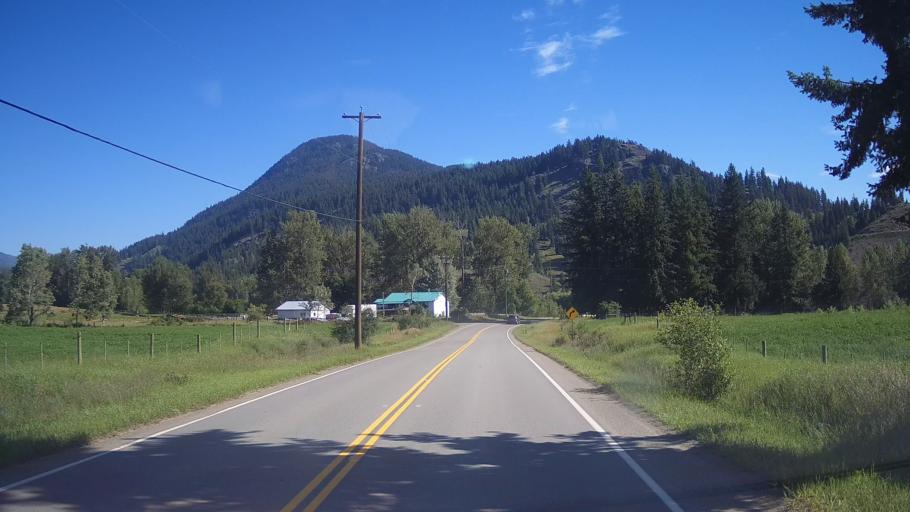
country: CA
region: British Columbia
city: Kamloops
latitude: 51.4300
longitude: -120.2102
